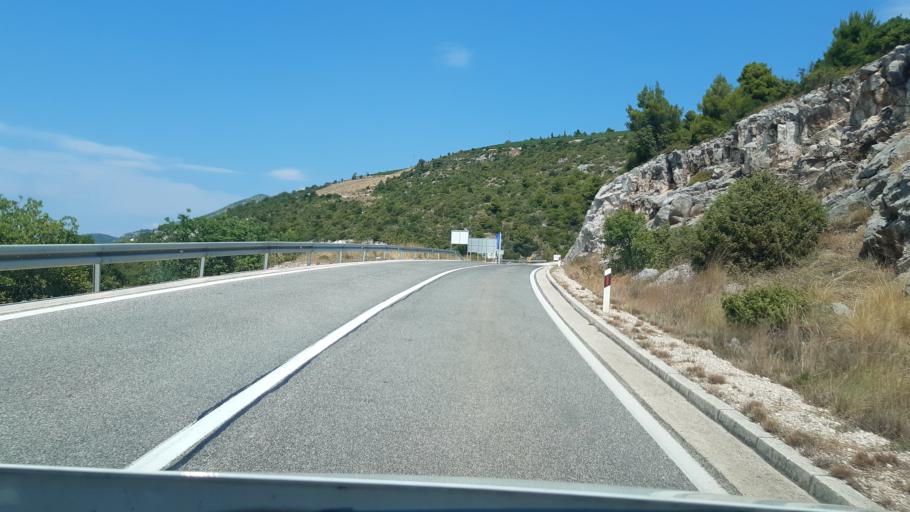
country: HR
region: Dubrovacko-Neretvanska
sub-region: Grad Dubrovnik
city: Opuzen
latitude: 42.9569
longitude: 17.5268
